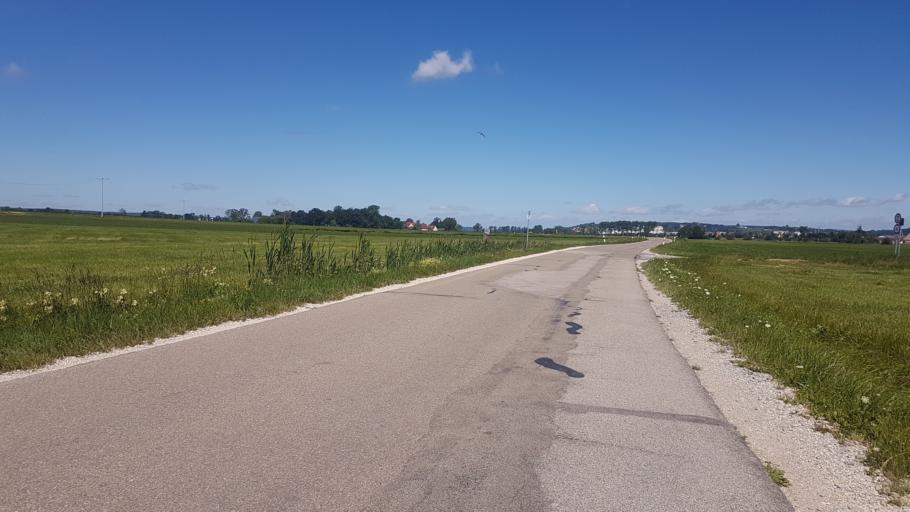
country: DE
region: Bavaria
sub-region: Regierungsbezirk Mittelfranken
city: Herrieden
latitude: 49.2118
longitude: 10.5282
